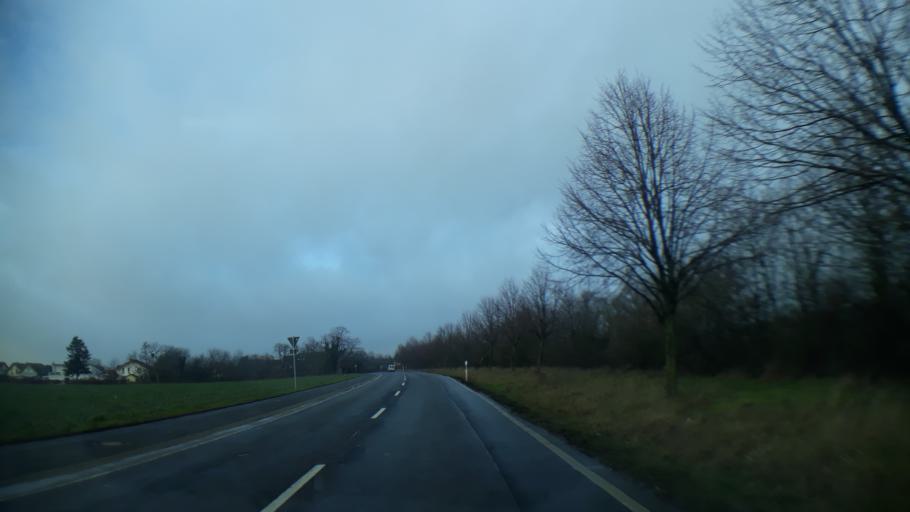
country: DE
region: North Rhine-Westphalia
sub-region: Regierungsbezirk Koln
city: Kreuzau
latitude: 50.7742
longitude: 6.4728
